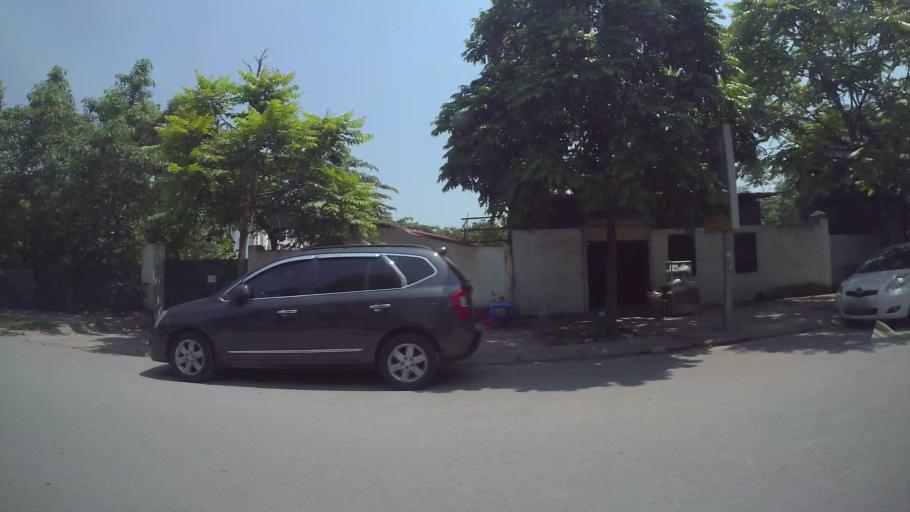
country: VN
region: Ha Noi
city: Hoan Kiem
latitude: 21.0416
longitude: 105.8825
